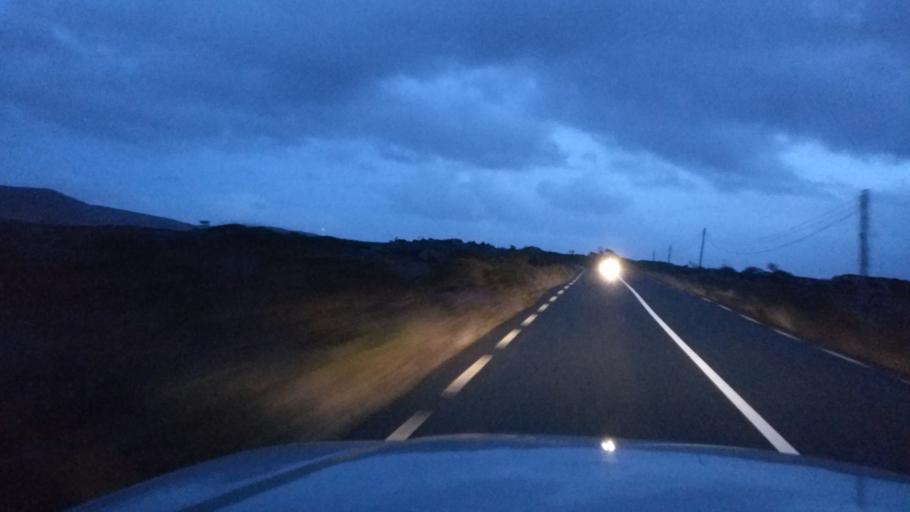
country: IE
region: Connaught
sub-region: County Galway
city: Oughterard
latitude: 53.3937
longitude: -9.5471
